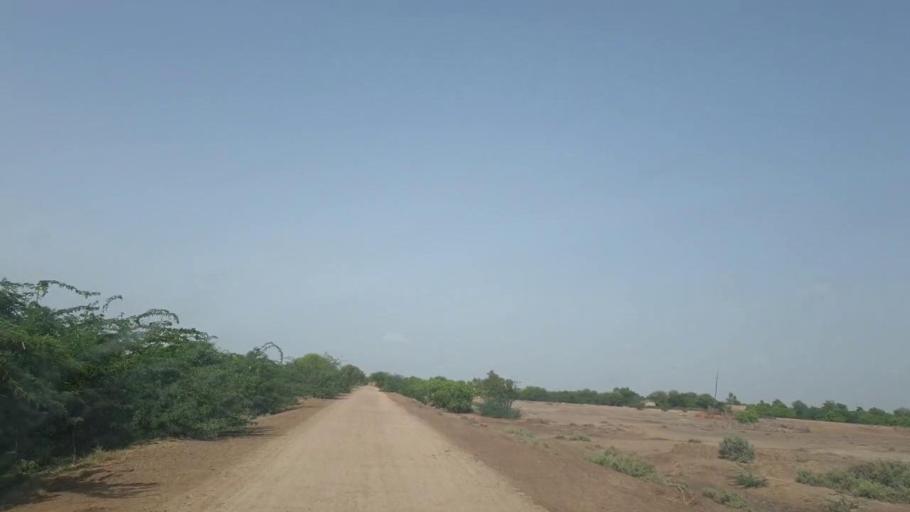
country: PK
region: Sindh
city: Tando Bago
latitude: 24.7960
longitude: 69.1531
